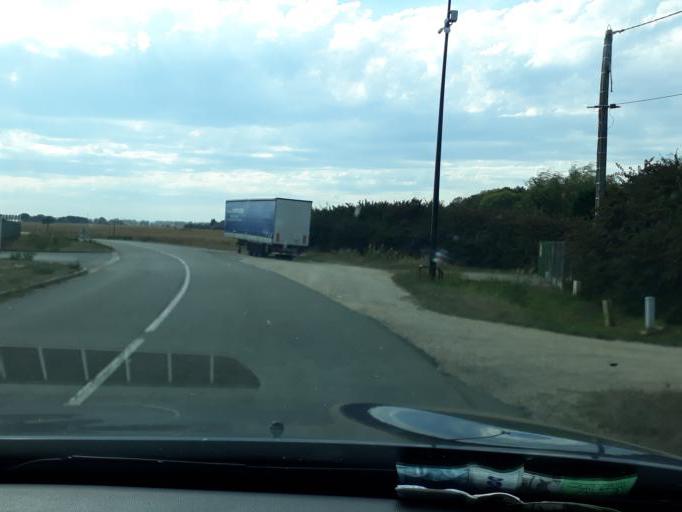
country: FR
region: Centre
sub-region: Departement du Loiret
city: Saint-Benoit-sur-Loire
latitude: 47.8402
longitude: 2.3177
